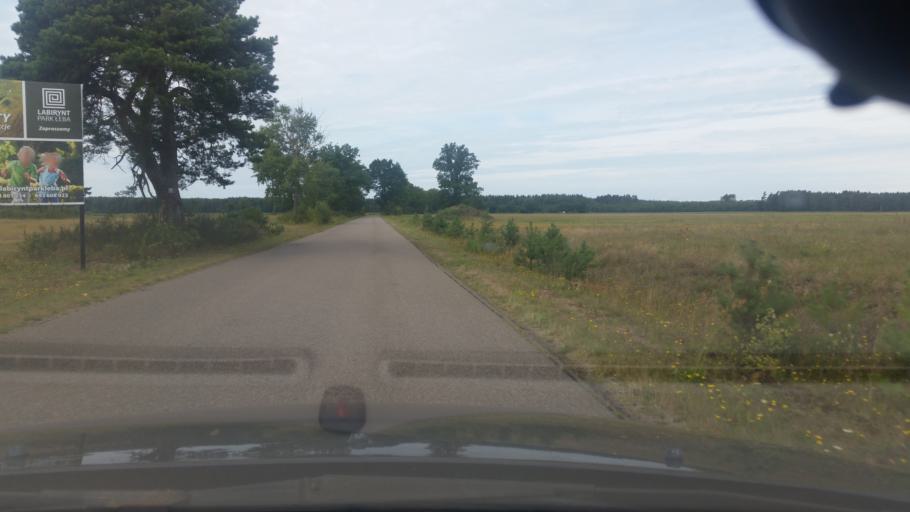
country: PL
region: Pomeranian Voivodeship
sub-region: Powiat leborski
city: Leba
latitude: 54.7315
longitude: 17.6065
